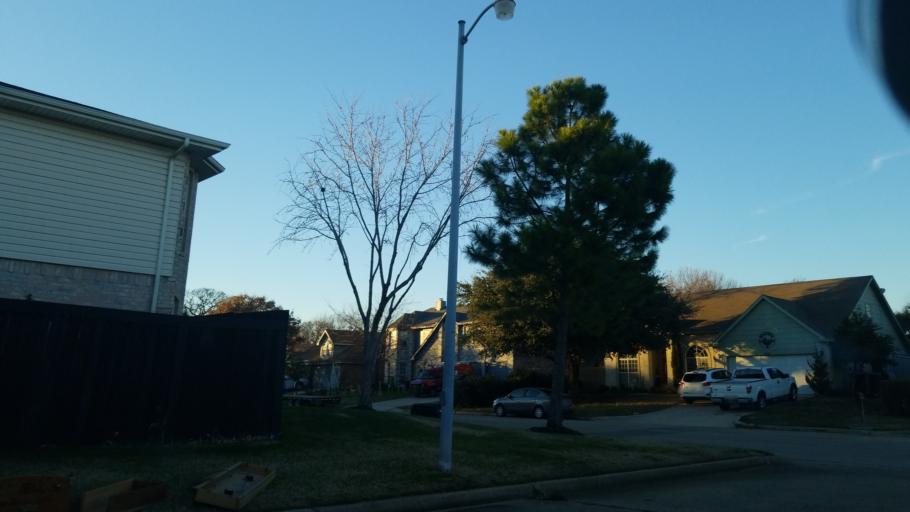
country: US
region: Texas
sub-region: Denton County
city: Hickory Creek
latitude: 33.1362
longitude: -97.0516
